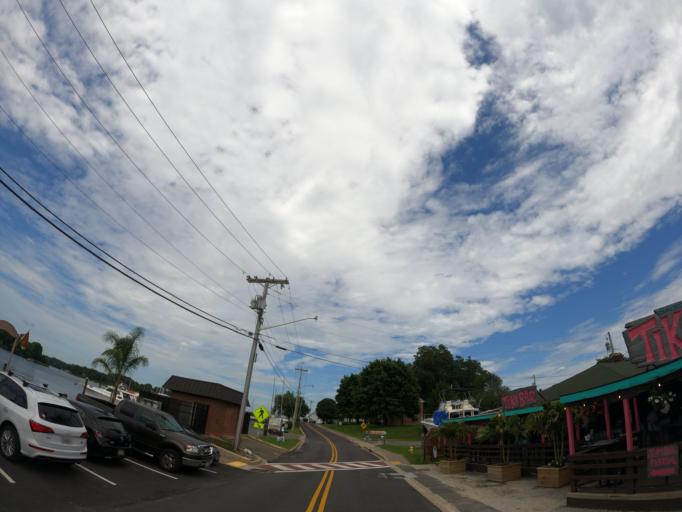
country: US
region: Maryland
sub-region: Calvert County
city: Solomons
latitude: 38.3197
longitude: -76.4563
